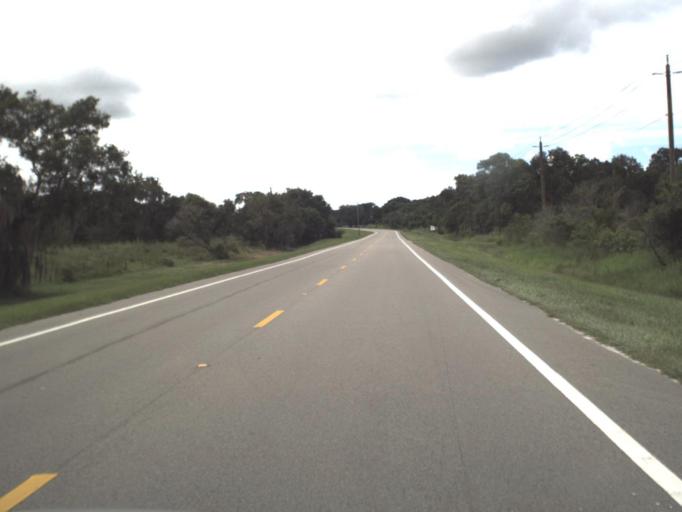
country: US
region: Florida
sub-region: Manatee County
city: Ellenton
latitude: 27.5874
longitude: -82.4136
